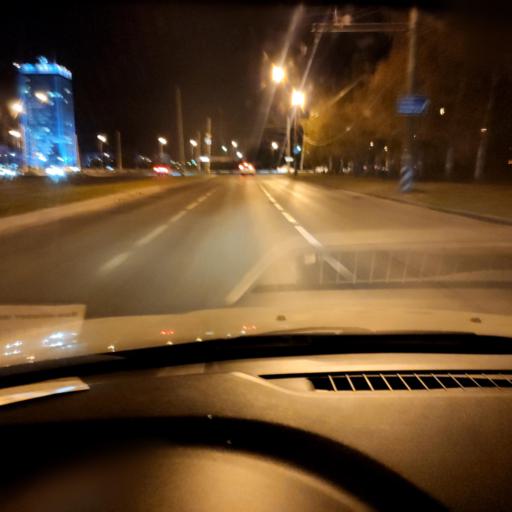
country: RU
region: Samara
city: Tol'yatti
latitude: 53.5506
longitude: 49.2667
